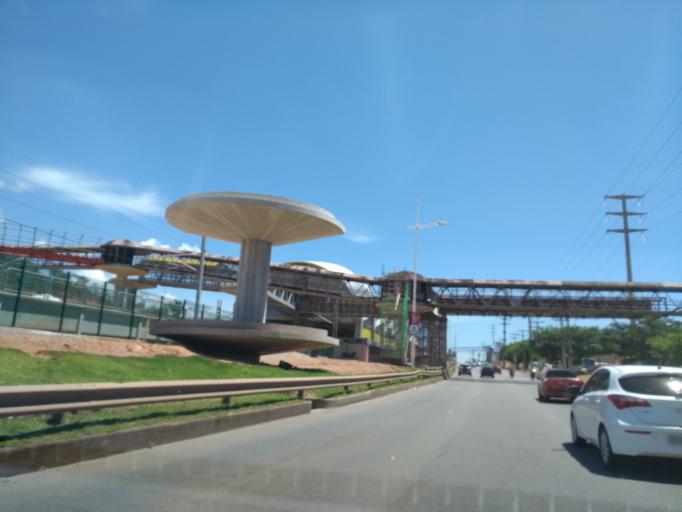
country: BR
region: Bahia
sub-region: Lauro De Freitas
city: Lauro de Freitas
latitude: -12.9357
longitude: -38.3954
